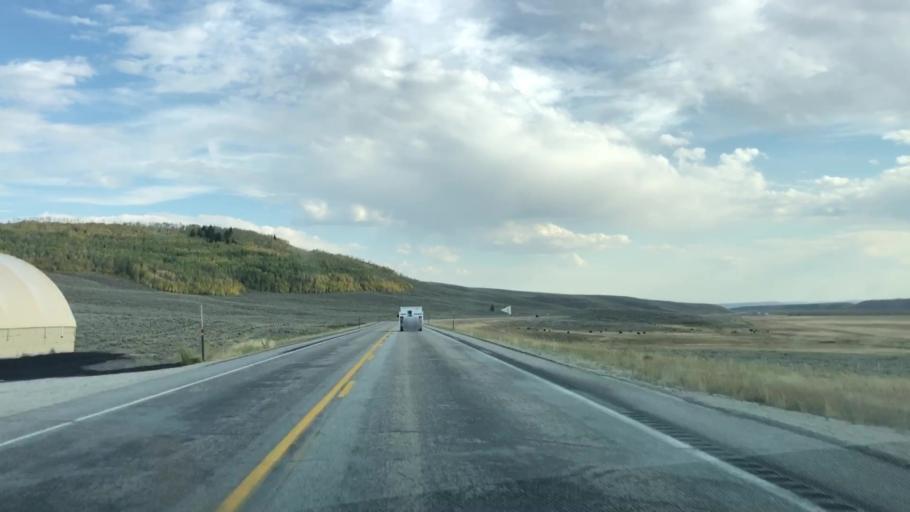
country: US
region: Wyoming
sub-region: Sublette County
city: Pinedale
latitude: 43.0892
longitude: -110.1642
